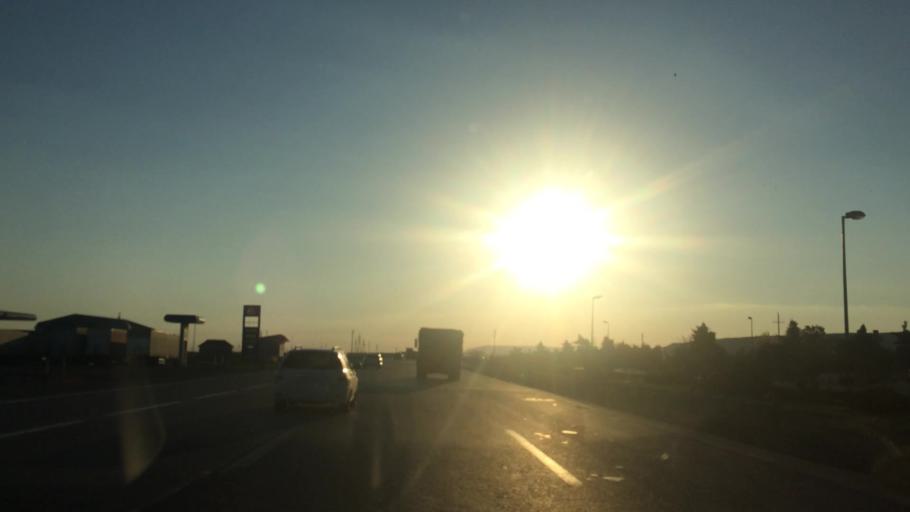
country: AZ
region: Baki
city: Qobustan
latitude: 39.9670
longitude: 49.4089
